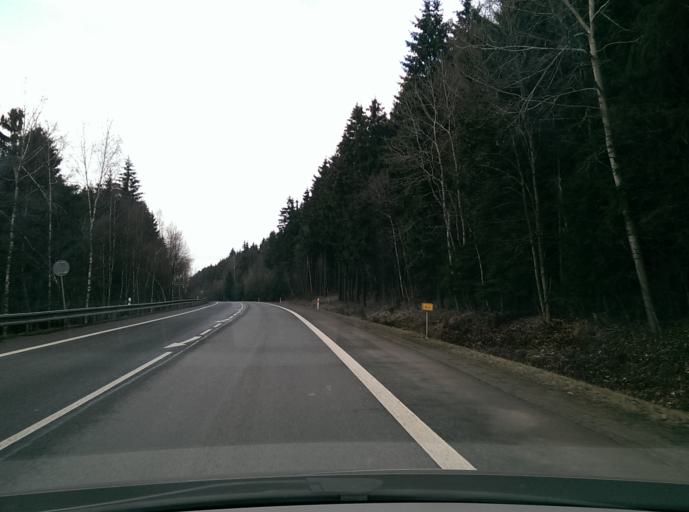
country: CZ
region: Liberecky
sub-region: Okres Jablonec nad Nisou
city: Jablonec nad Nisou
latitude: 50.7015
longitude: 15.1500
